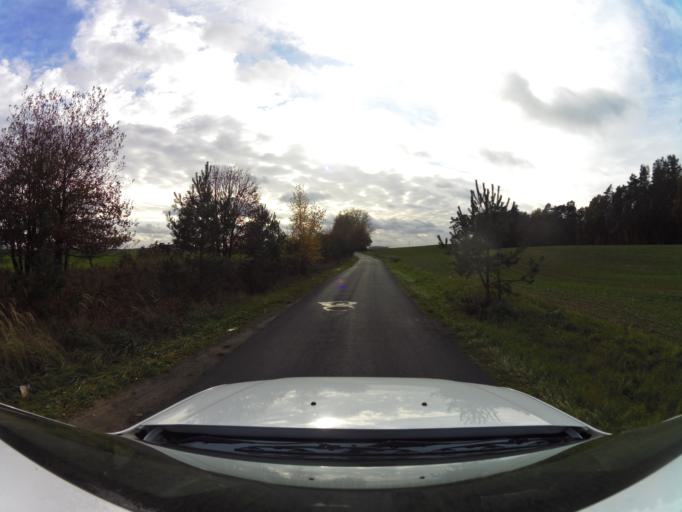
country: PL
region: West Pomeranian Voivodeship
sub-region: Powiat gryficki
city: Gryfice
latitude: 53.9037
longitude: 15.1339
